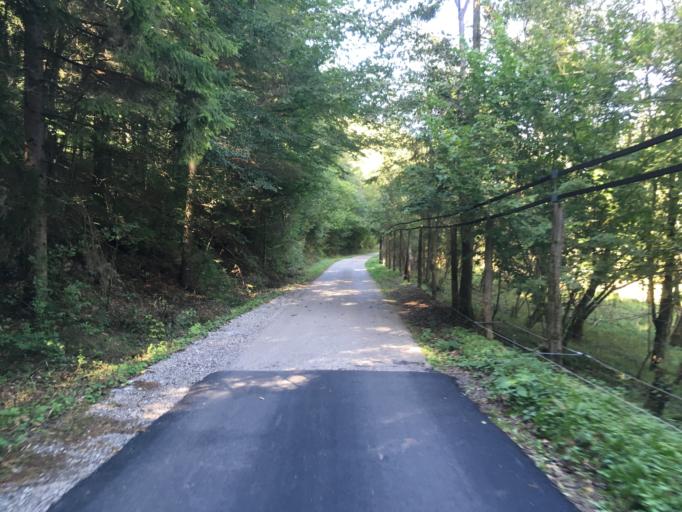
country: SK
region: Trenciansky
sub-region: Okres Povazska Bystrica
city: Povazska Bystrica
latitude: 49.0199
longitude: 18.4390
